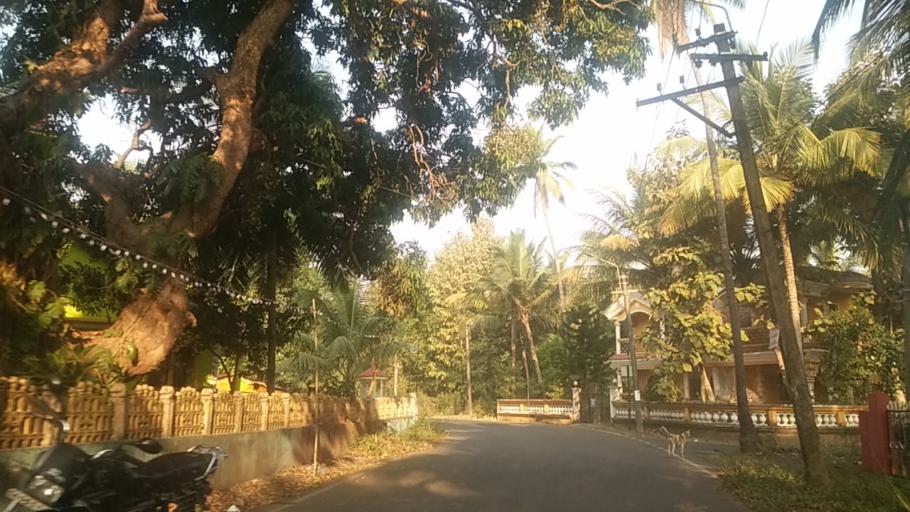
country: IN
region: Goa
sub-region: South Goa
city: Chinchinim
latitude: 15.2325
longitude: 73.9918
